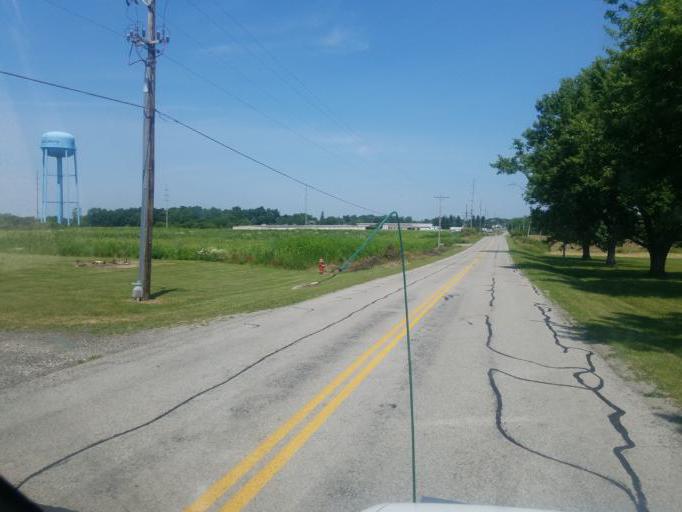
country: US
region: Ohio
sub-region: Logan County
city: West Liberty
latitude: 40.2613
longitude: -83.7583
